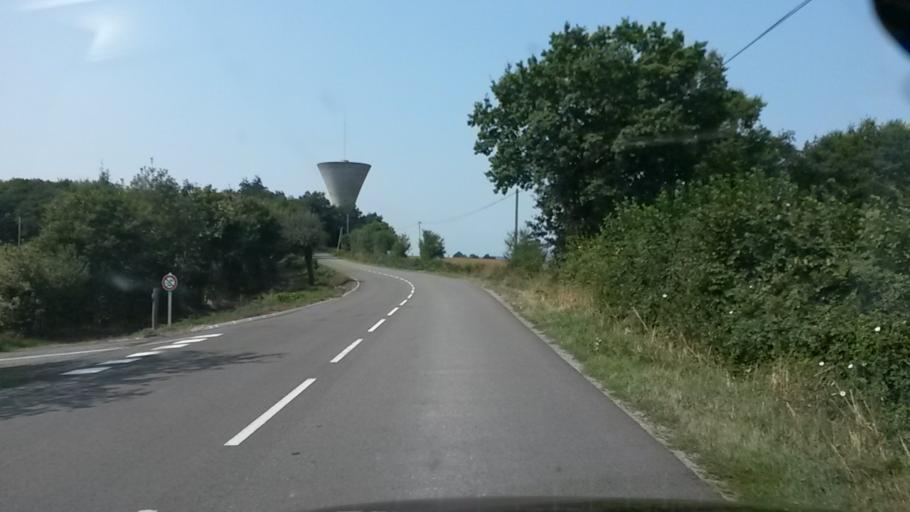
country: FR
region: Pays de la Loire
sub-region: Departement de la Mayenne
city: Villaines-la-Juhel
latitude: 48.3535
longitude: -0.2550
